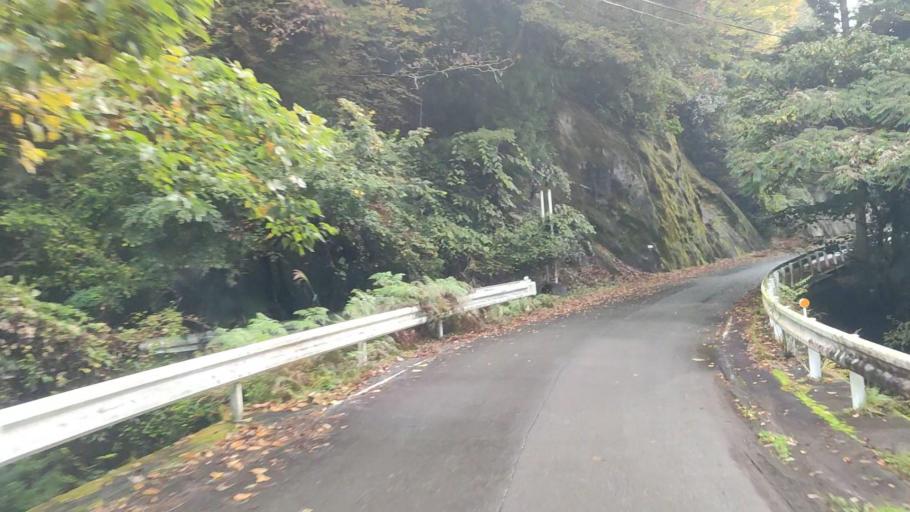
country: JP
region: Shizuoka
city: Fujinomiya
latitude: 35.3252
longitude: 138.4347
